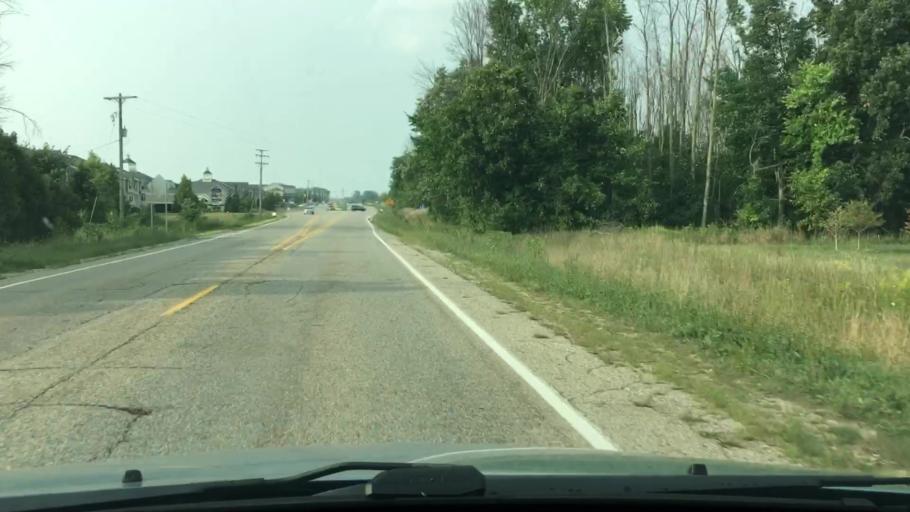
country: US
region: Michigan
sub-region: Ottawa County
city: Allendale
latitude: 42.9537
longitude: -85.9038
